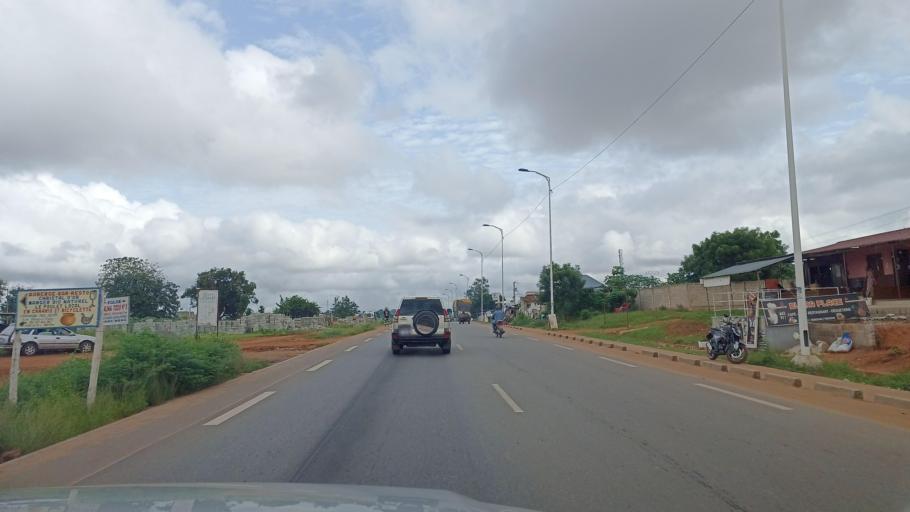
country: TG
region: Maritime
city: Tsevie
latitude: 6.3404
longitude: 1.2152
